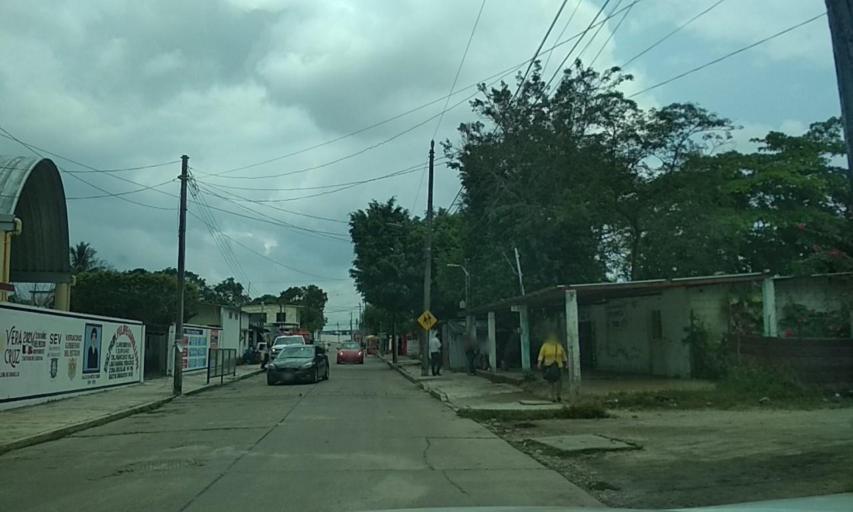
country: MX
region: Veracruz
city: Las Choapas
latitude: 17.8983
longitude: -94.0920
